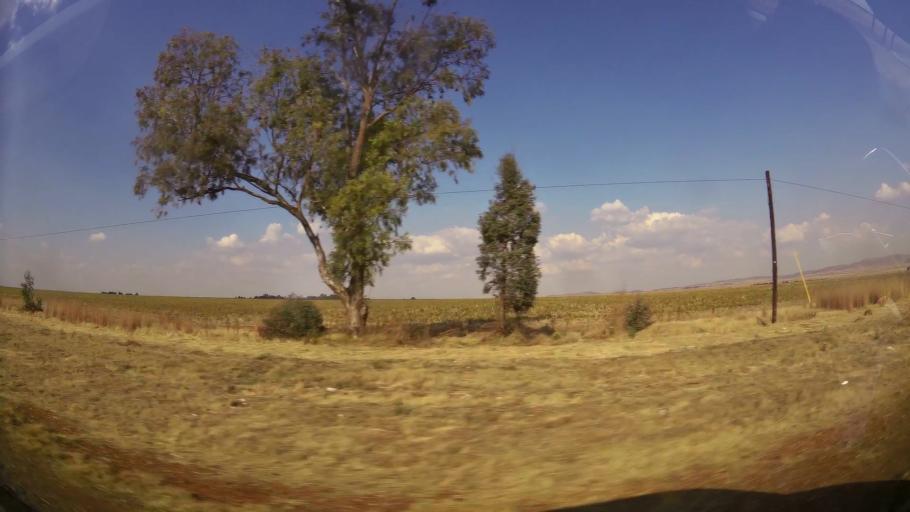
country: ZA
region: Gauteng
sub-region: Sedibeng District Municipality
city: Heidelberg
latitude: -26.3965
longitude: 28.2886
